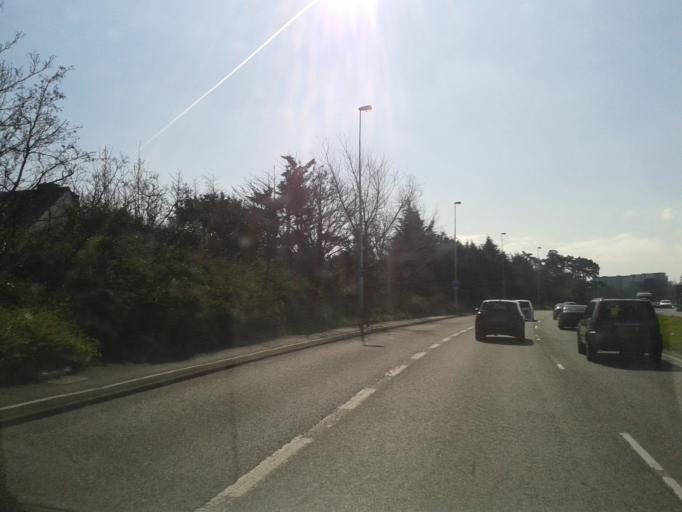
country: IE
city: Booterstown
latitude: 53.2881
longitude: -6.1945
